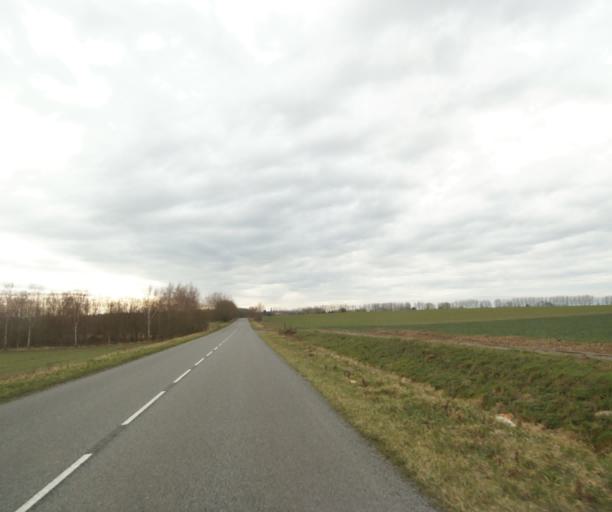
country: FR
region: Nord-Pas-de-Calais
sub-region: Departement du Nord
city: Jenlain
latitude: 50.3252
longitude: 3.6328
